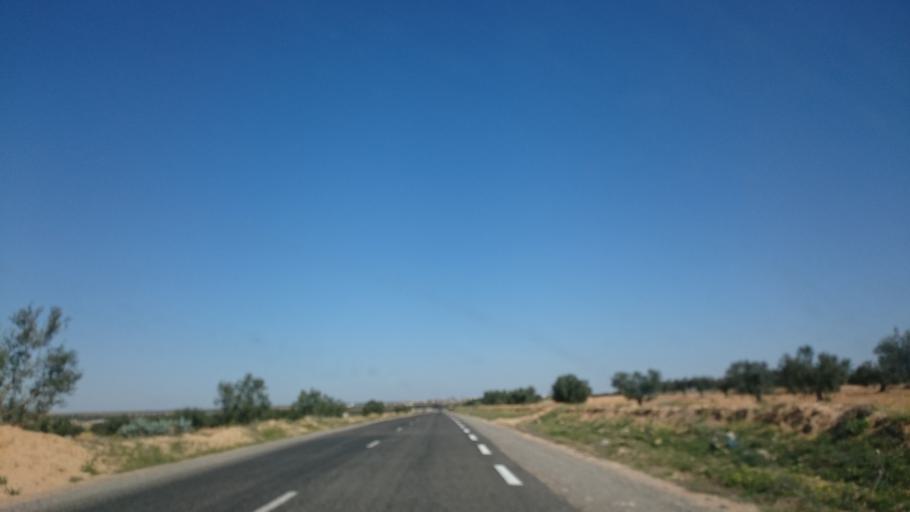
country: TN
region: Safaqis
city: Sfax
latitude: 34.7880
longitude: 10.4988
